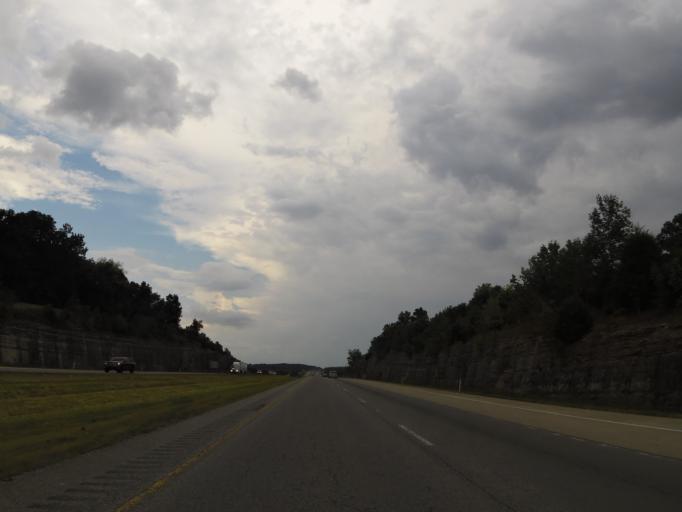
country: US
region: Tennessee
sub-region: Wilson County
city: Rural Hill
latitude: 36.0318
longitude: -86.4288
